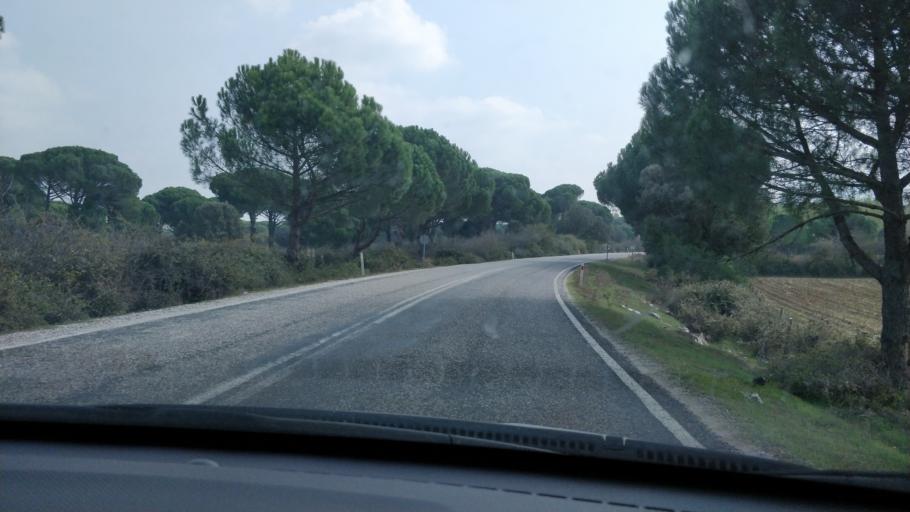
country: TR
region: Izmir
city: Kozak
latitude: 39.2606
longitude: 27.0354
